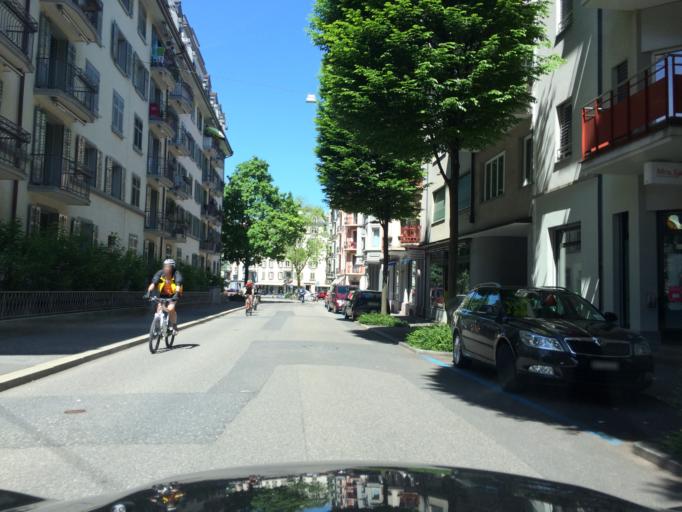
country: CH
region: Lucerne
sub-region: Lucerne-Stadt District
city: Luzern
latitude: 47.0443
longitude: 8.3072
